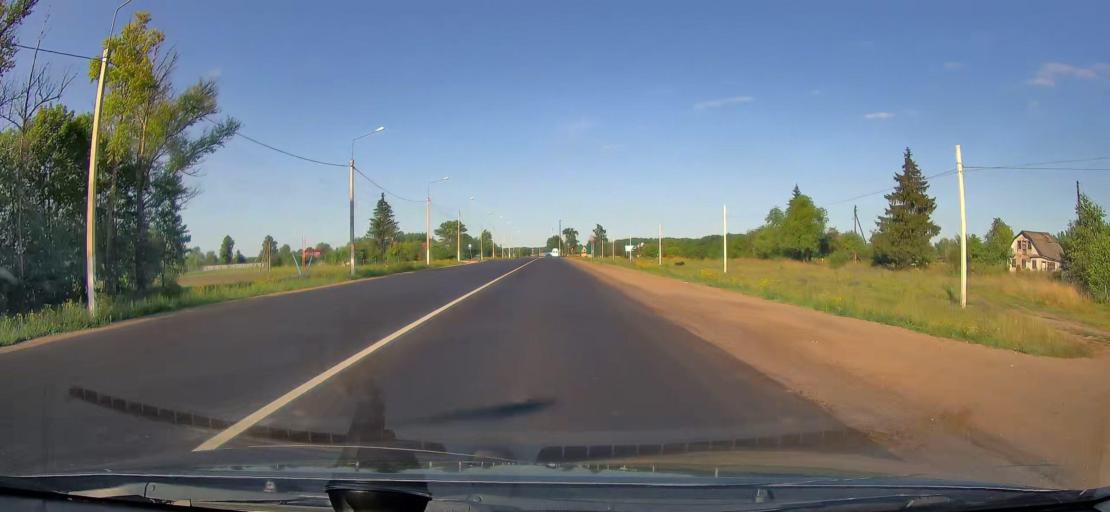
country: RU
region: Tula
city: Bol'shoye Skuratovo
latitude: 53.4336
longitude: 36.8050
